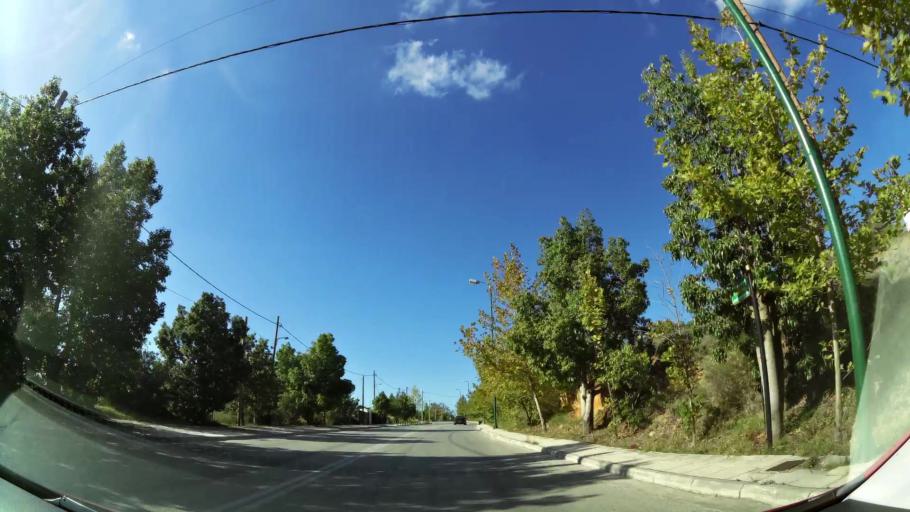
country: GR
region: Attica
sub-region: Nomarchia Anatolikis Attikis
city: Anthousa
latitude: 38.0199
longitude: 23.8724
